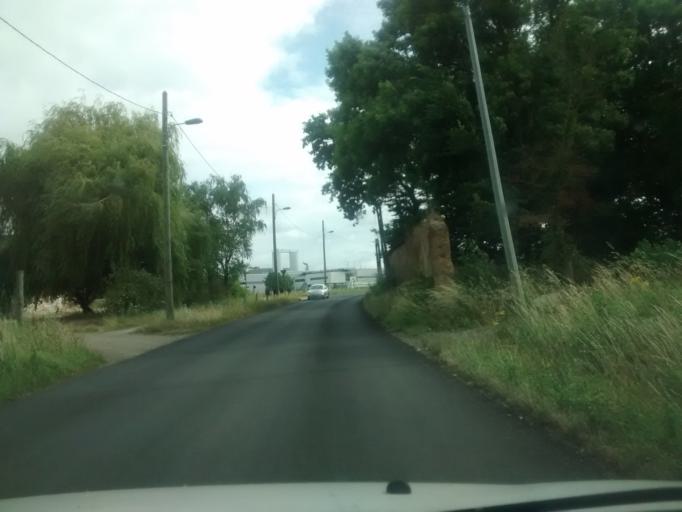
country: FR
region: Brittany
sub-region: Departement d'Ille-et-Vilaine
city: Vezin-le-Coquet
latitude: 48.0960
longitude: -1.7323
